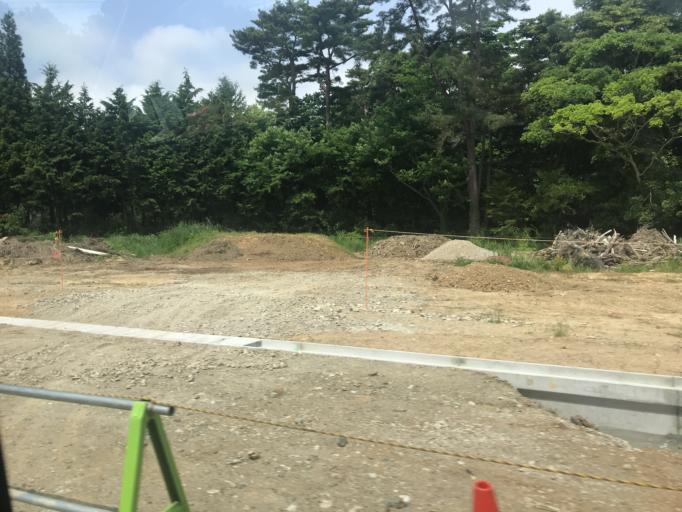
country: JP
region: Fukushima
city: Namie
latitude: 37.2987
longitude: 141.0186
